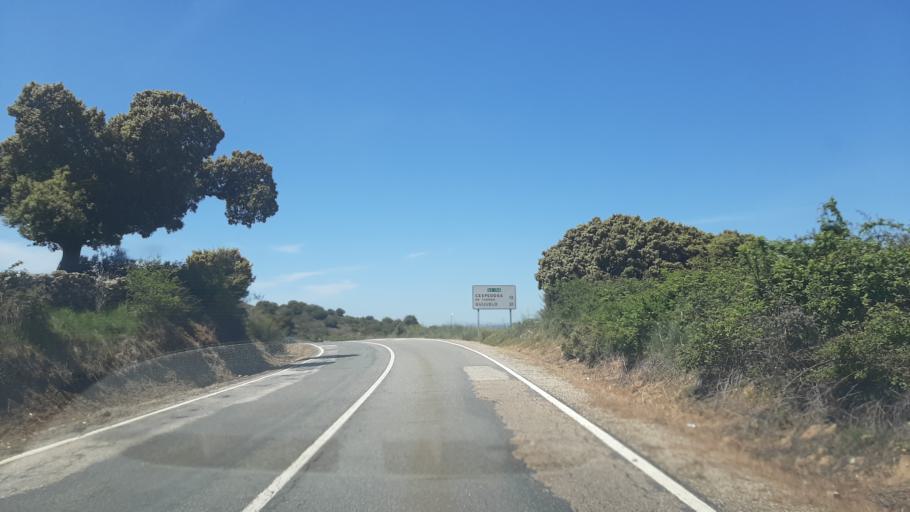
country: ES
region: Castille and Leon
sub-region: Provincia de Avila
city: Narrillos del Alamo
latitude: 40.5343
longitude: -5.4552
